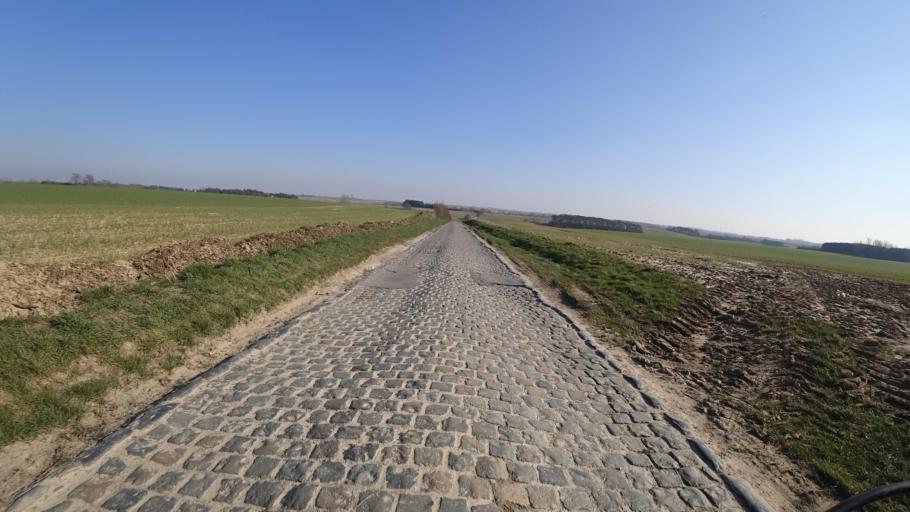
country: BE
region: Wallonia
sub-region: Province du Brabant Wallon
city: Court-Saint-Etienne
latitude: 50.6085
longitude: 4.5895
